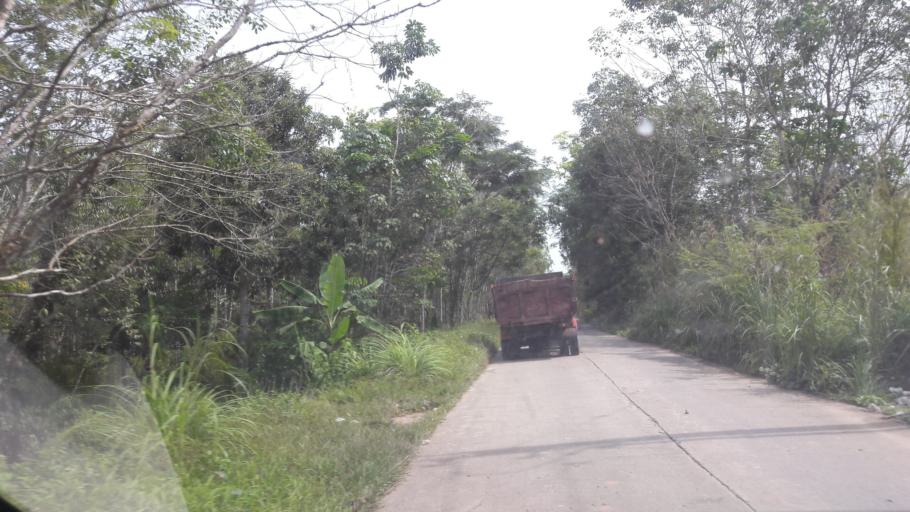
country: ID
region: South Sumatra
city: Gunungmenang
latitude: -3.2453
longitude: 104.1347
